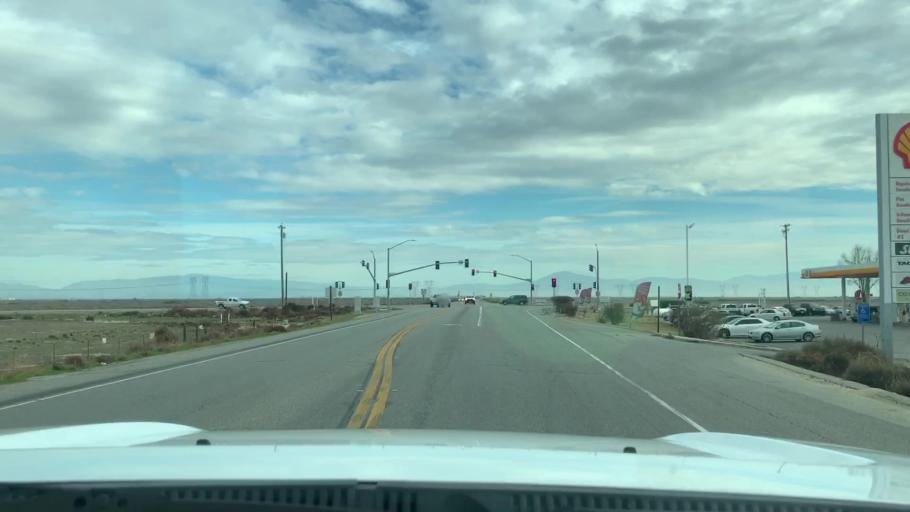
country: US
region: California
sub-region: Kern County
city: Rosedale
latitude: 35.2674
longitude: -119.2541
